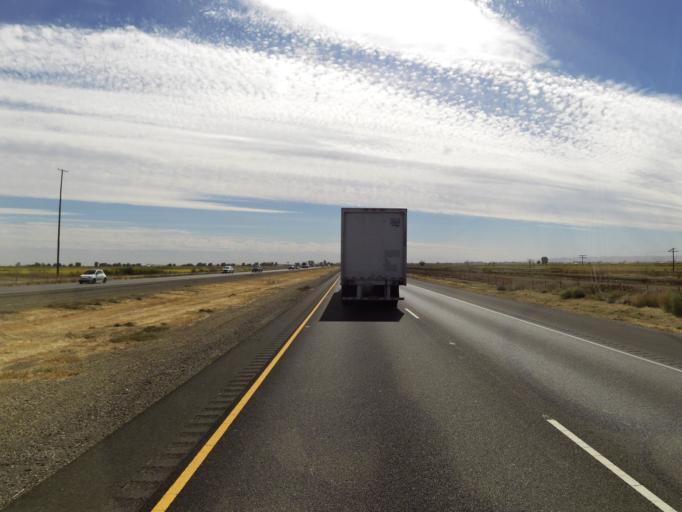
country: US
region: California
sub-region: Colusa County
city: Williams
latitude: 39.1902
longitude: -122.1696
